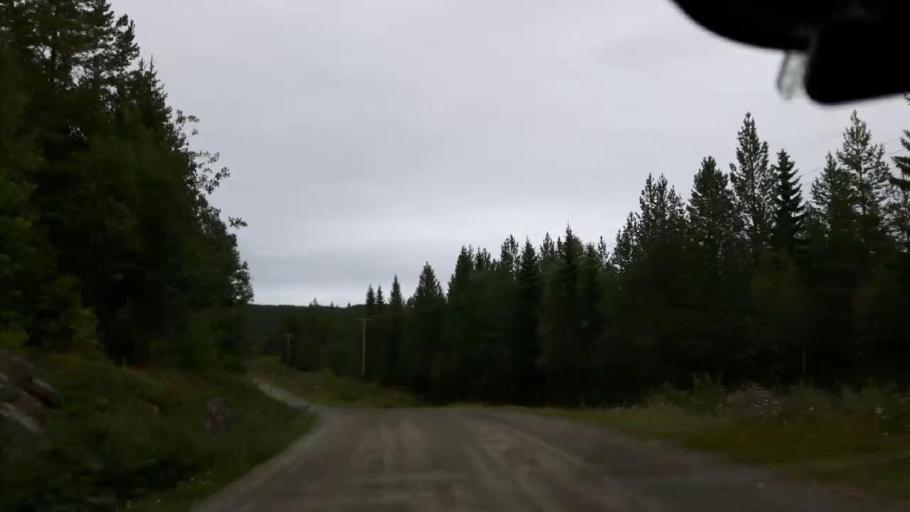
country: SE
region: Vaesternorrland
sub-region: Ange Kommun
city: Fransta
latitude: 62.8593
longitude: 15.9830
